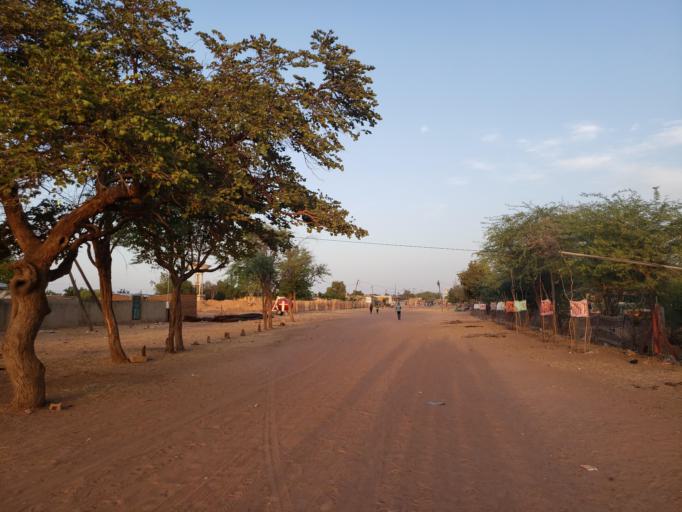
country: SN
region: Matam
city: Ranerou
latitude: 15.2969
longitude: -13.9645
